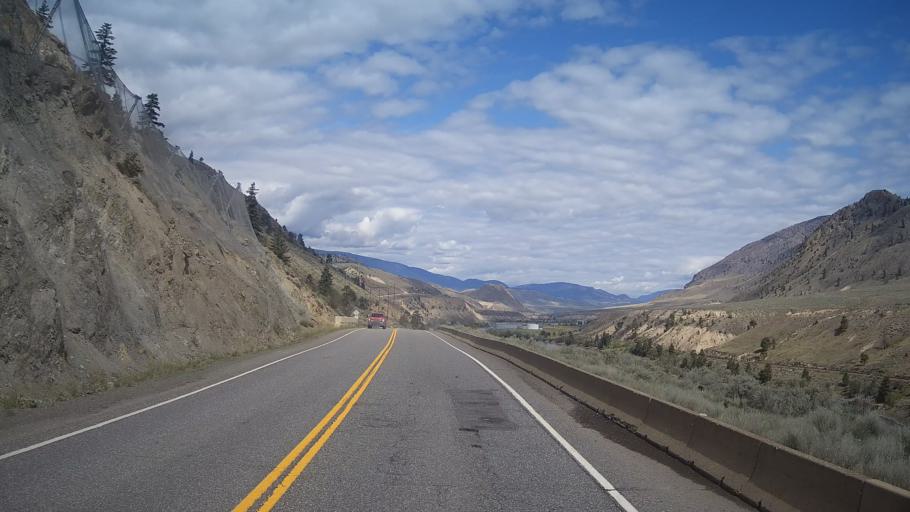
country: CA
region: British Columbia
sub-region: Thompson-Nicola Regional District
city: Ashcroft
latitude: 50.5403
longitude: -121.2887
